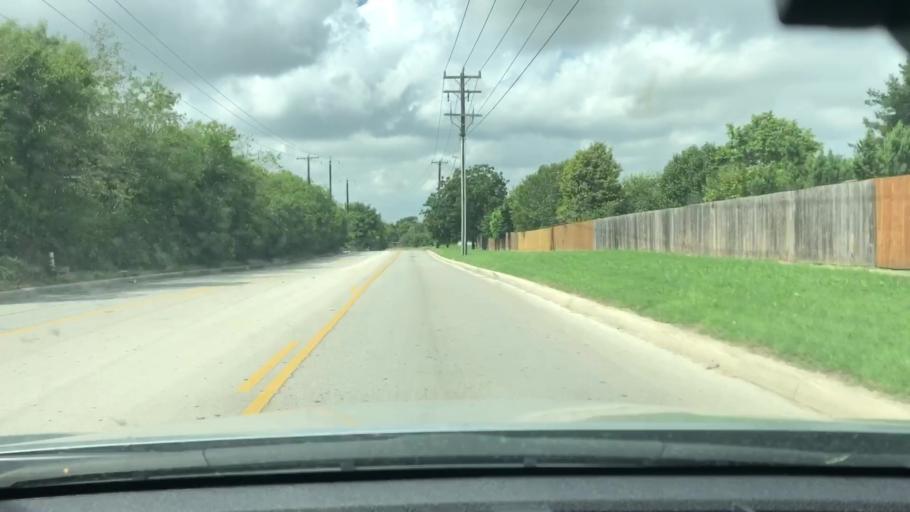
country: US
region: Texas
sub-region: Bexar County
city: Windcrest
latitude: 29.5315
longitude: -98.3754
